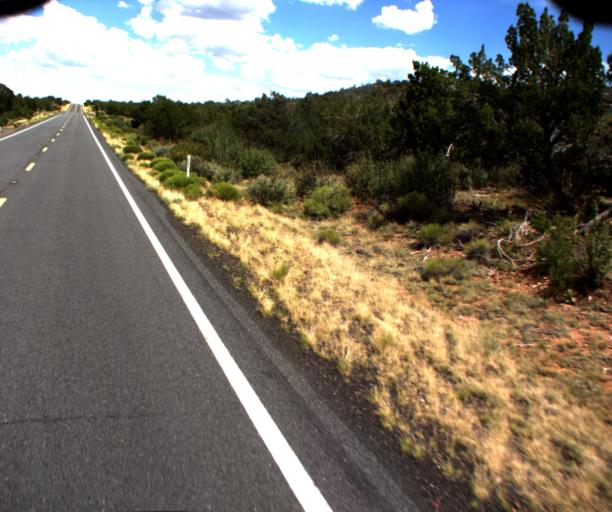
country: US
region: Arizona
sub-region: Coconino County
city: Parks
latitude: 35.5639
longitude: -111.9001
